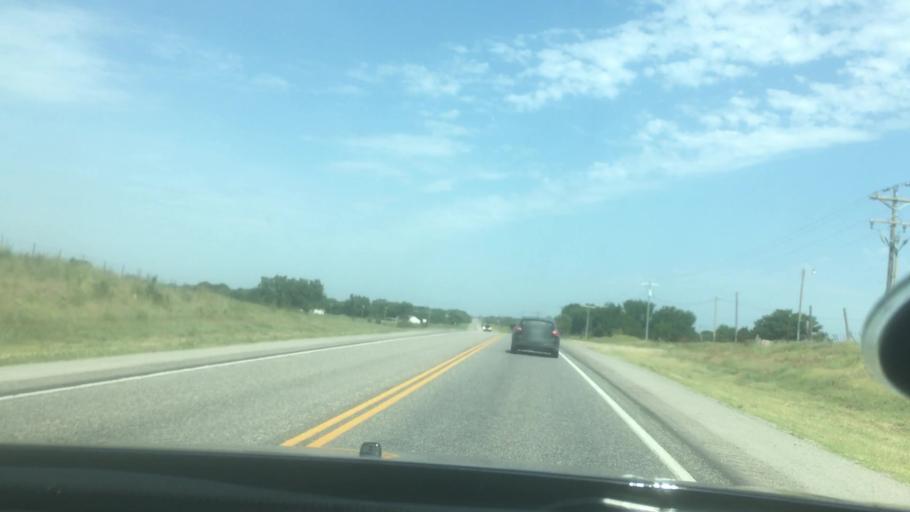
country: US
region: Oklahoma
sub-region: Seminole County
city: Konawa
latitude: 34.8671
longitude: -96.8340
